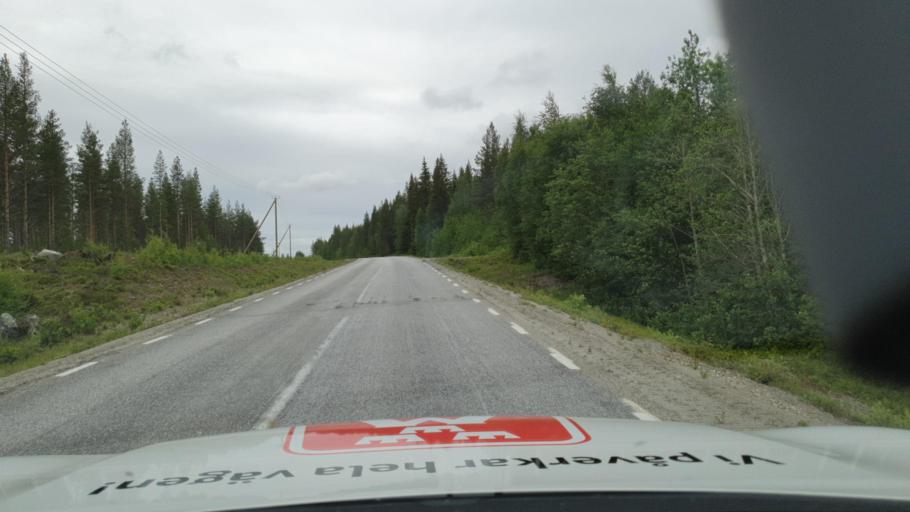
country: SE
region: Vaesterbotten
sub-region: Lycksele Kommun
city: Lycksele
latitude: 64.1505
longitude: 18.3601
